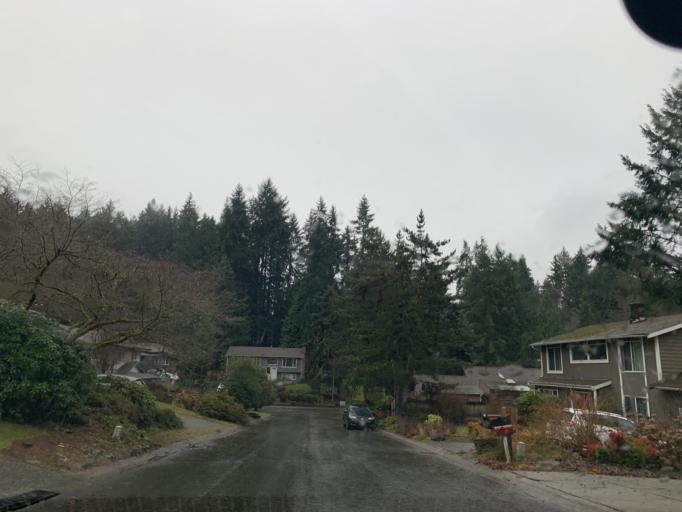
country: US
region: Washington
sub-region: King County
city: Kingsgate
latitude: 47.7358
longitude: -122.1815
